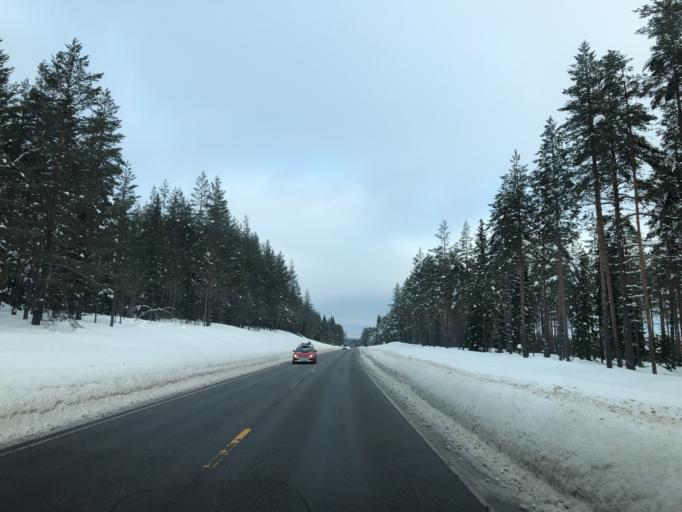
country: NO
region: Hedmark
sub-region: Trysil
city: Innbygda
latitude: 61.1838
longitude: 12.1908
